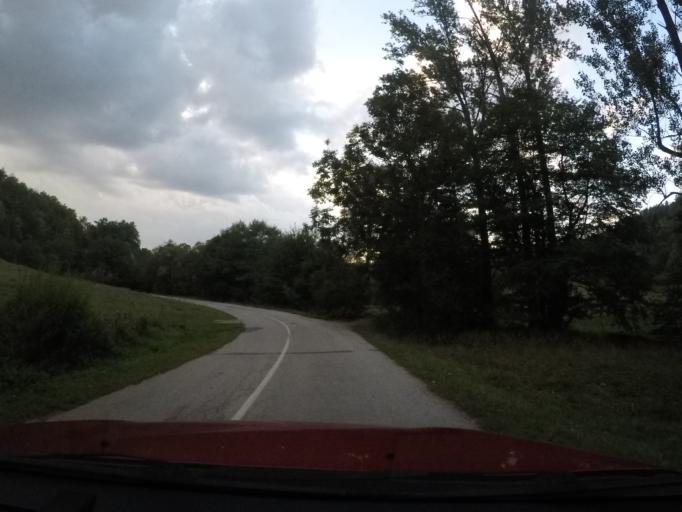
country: SK
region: Kosicky
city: Medzev
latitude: 48.6319
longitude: 20.7309
